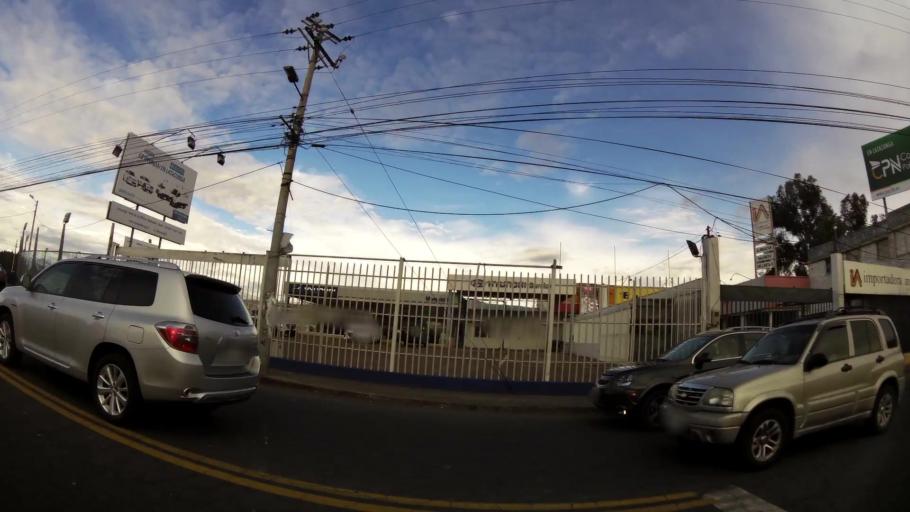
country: EC
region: Cotopaxi
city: Latacunga
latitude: -0.9268
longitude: -78.6249
